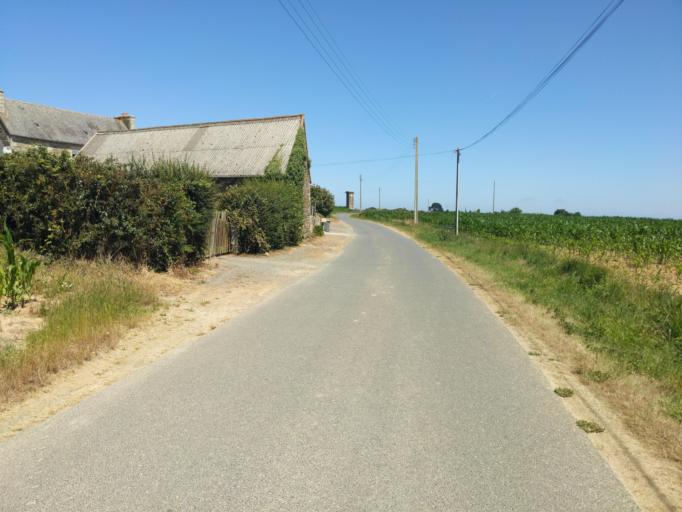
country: FR
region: Brittany
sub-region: Departement des Cotes-d'Armor
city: Plouguiel
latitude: 48.8039
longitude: -3.2255
